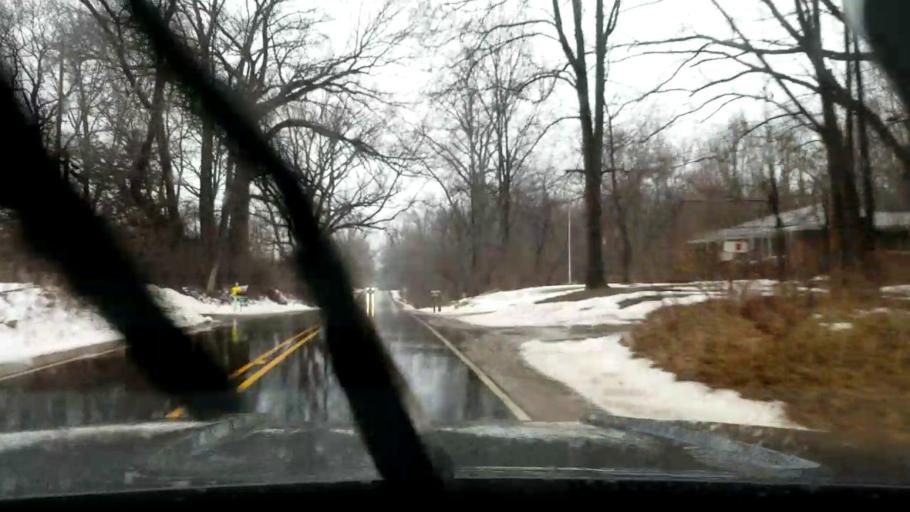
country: US
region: Michigan
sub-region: Jackson County
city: Grass Lake
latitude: 42.3212
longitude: -84.2648
